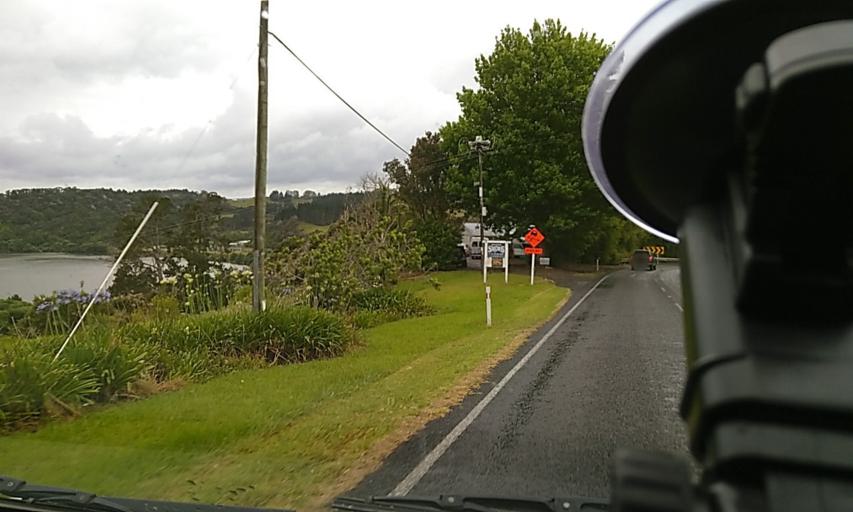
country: NZ
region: Auckland
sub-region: Auckland
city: Pukekohe East
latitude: -37.2977
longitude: 174.9414
